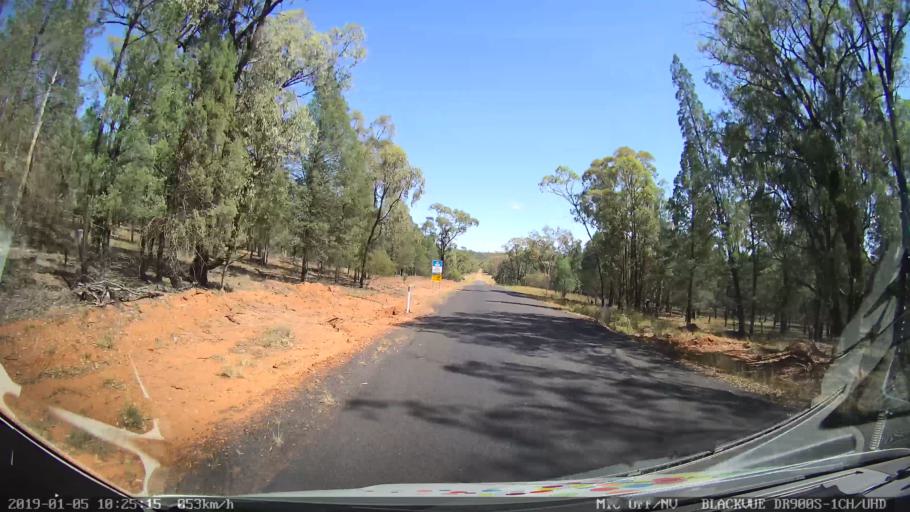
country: AU
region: New South Wales
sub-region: Gilgandra
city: Gilgandra
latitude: -31.5627
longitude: 148.9603
